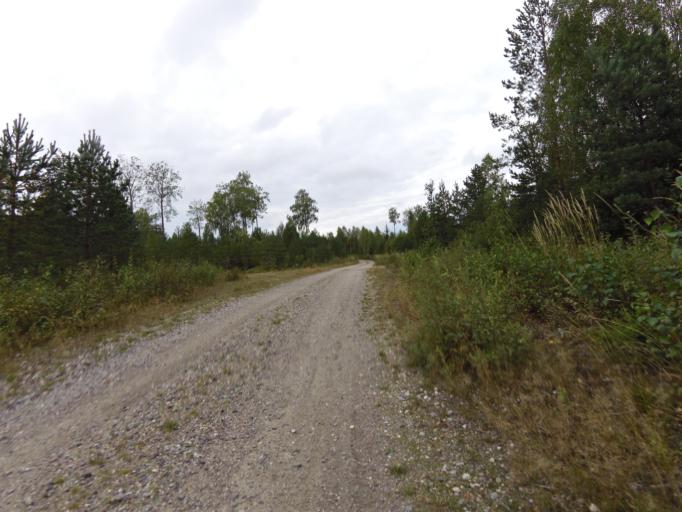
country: SE
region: Gaevleborg
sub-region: Gavle Kommun
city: Valbo
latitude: 60.7442
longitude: 17.0224
